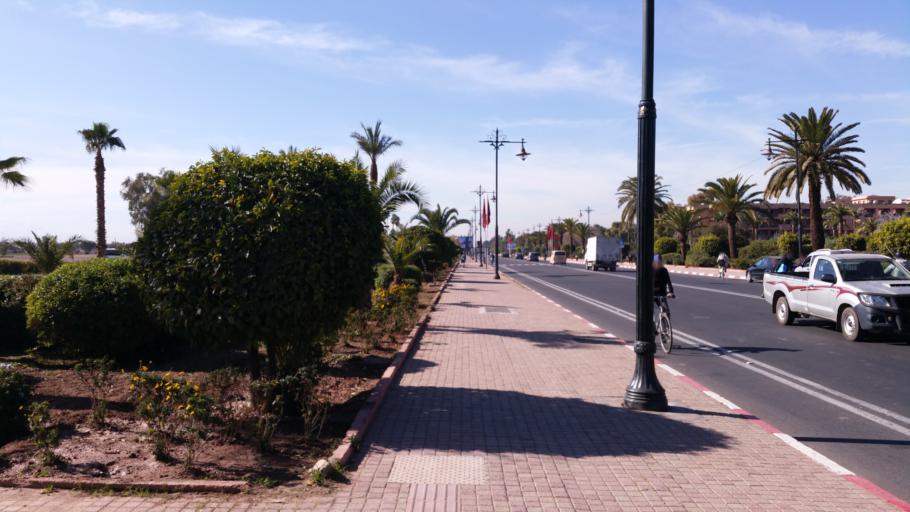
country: MA
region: Marrakech-Tensift-Al Haouz
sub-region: Marrakech
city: Marrakesh
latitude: 31.6212
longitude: -8.0001
